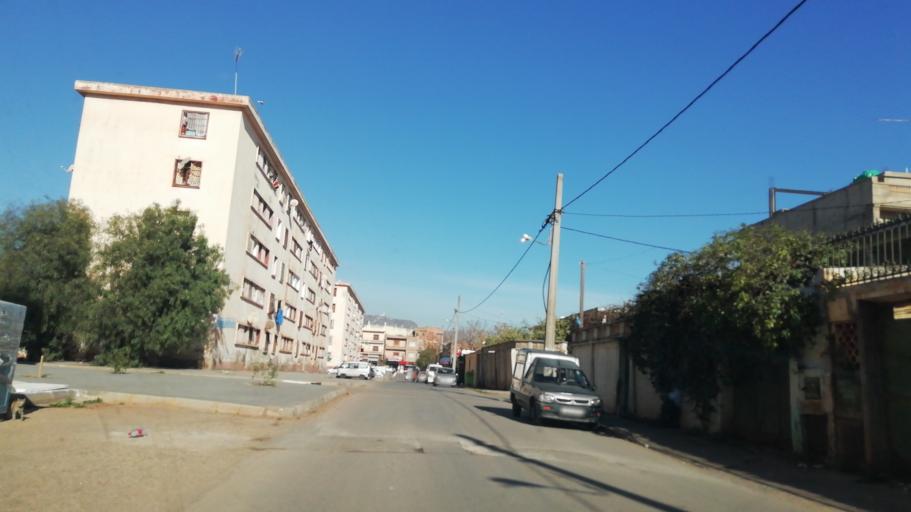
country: DZ
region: Oran
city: Oran
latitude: 35.6724
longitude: -0.6487
